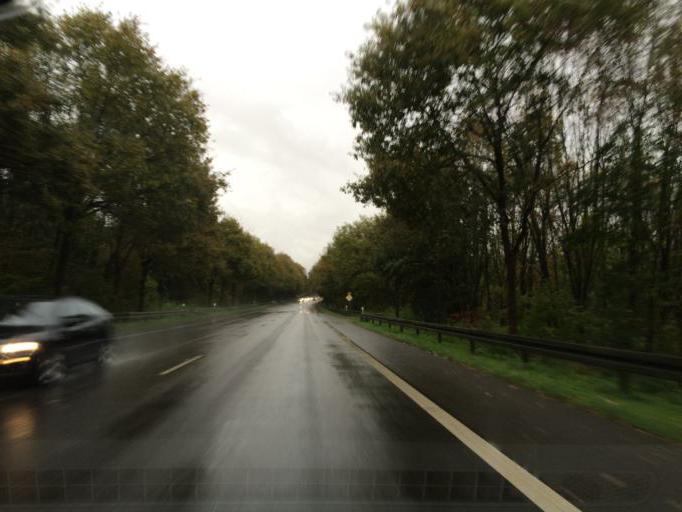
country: DE
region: North Rhine-Westphalia
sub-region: Regierungsbezirk Munster
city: Haltern
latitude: 51.7316
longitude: 7.1390
